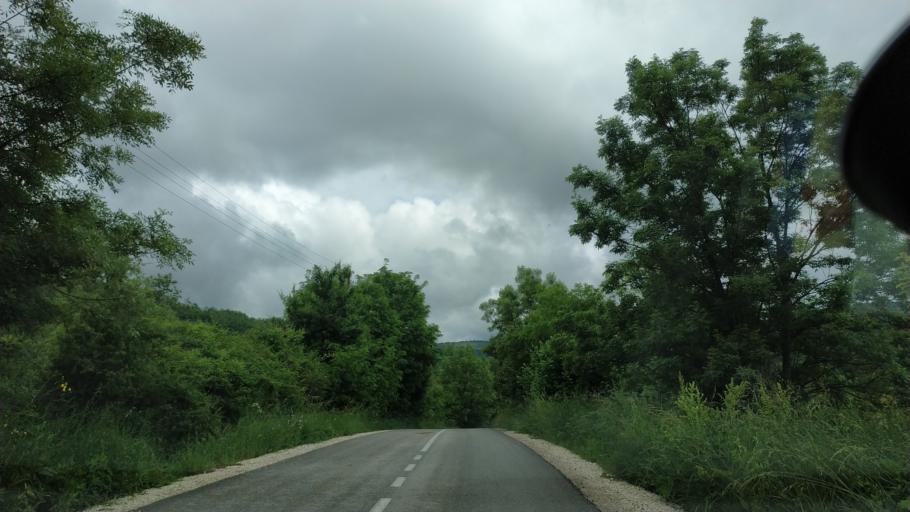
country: RS
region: Central Serbia
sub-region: Zajecarski Okrug
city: Soko Banja
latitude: 43.6566
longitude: 21.9047
